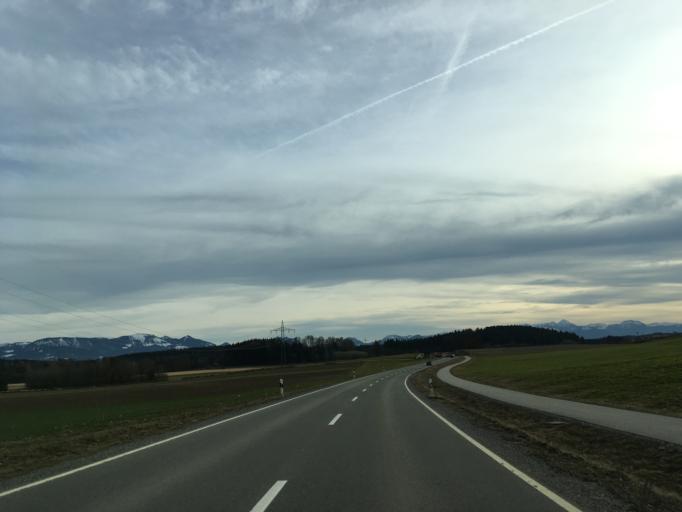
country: DE
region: Bavaria
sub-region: Upper Bavaria
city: Sochtenau
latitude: 47.9203
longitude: 12.2180
